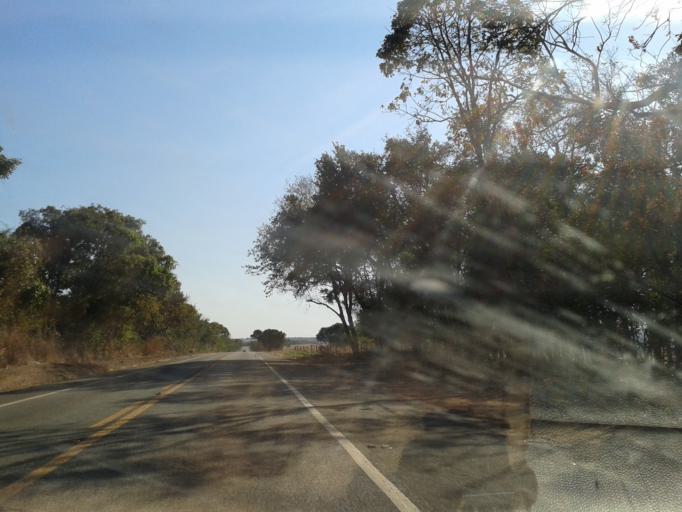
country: BR
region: Goias
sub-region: Mozarlandia
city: Mozarlandia
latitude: -14.8558
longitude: -50.5455
